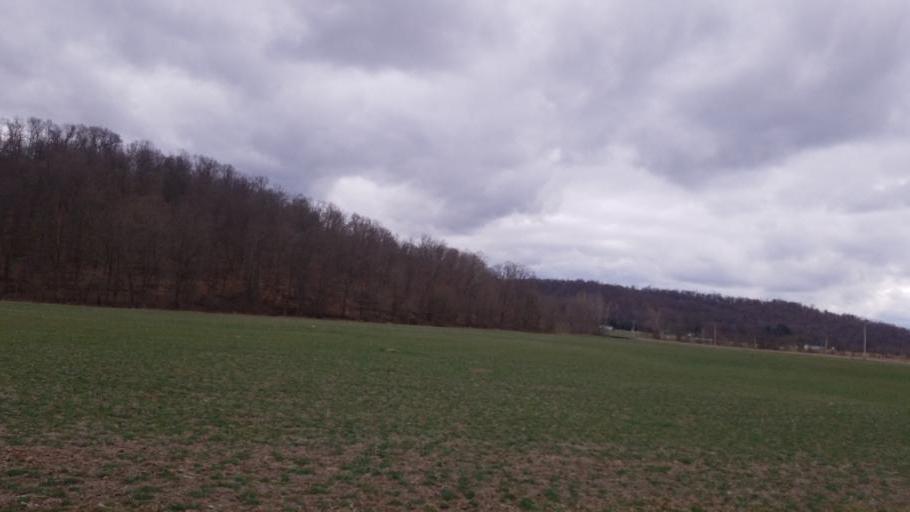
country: US
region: Ohio
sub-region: Licking County
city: Newark
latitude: 40.1622
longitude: -82.2915
